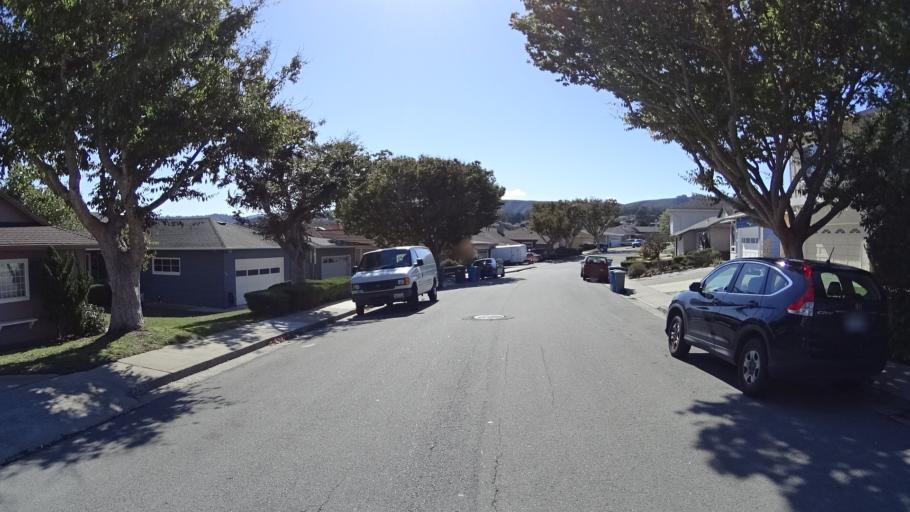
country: US
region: California
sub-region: San Mateo County
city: San Bruno
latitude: 37.6214
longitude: -122.4312
